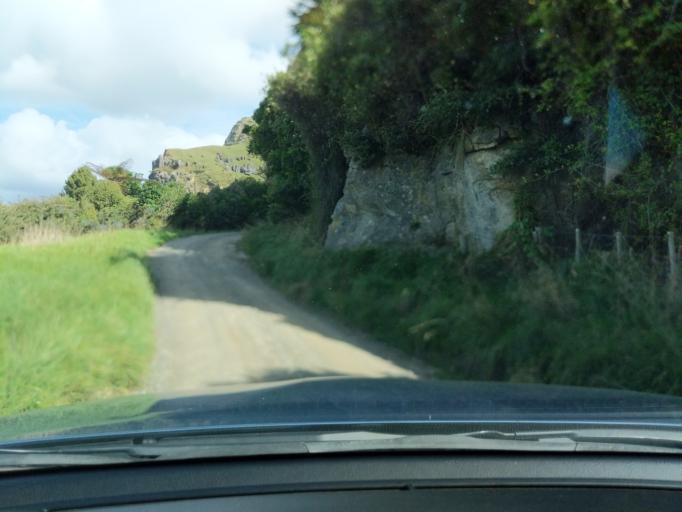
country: NZ
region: Tasman
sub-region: Tasman District
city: Takaka
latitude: -40.6441
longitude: 172.4318
